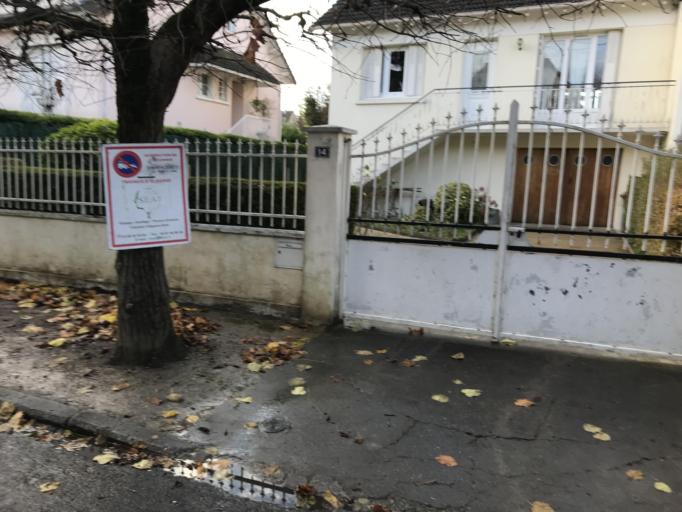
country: FR
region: Ile-de-France
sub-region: Departement de Seine-Saint-Denis
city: Gournay-sur-Marne
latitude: 48.8633
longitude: 2.5702
